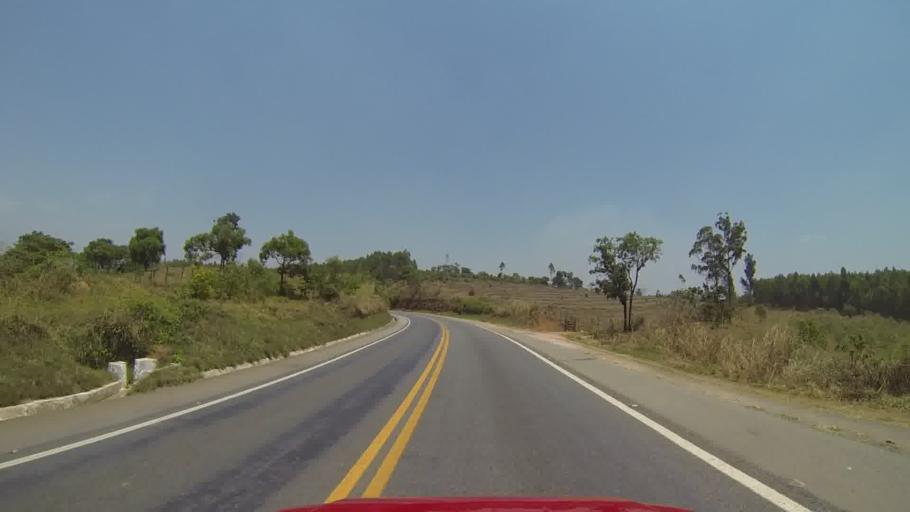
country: BR
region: Minas Gerais
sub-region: Itapecerica
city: Itapecerica
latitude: -20.3107
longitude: -45.2207
